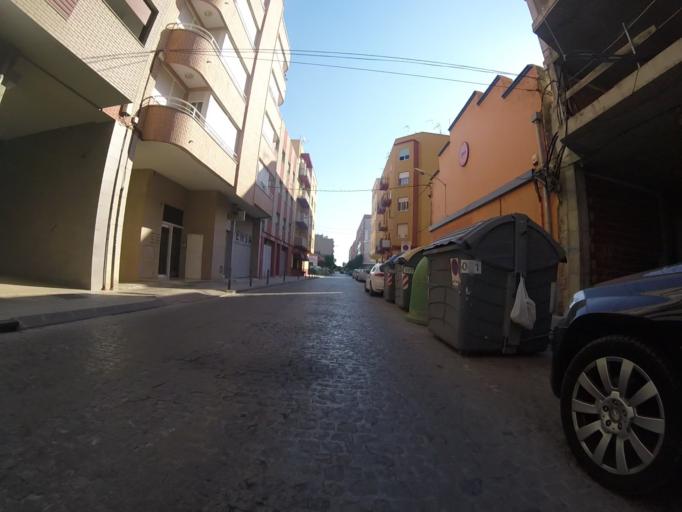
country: ES
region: Valencia
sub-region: Provincia de Castello
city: Benicarlo
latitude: 40.4216
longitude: 0.4277
